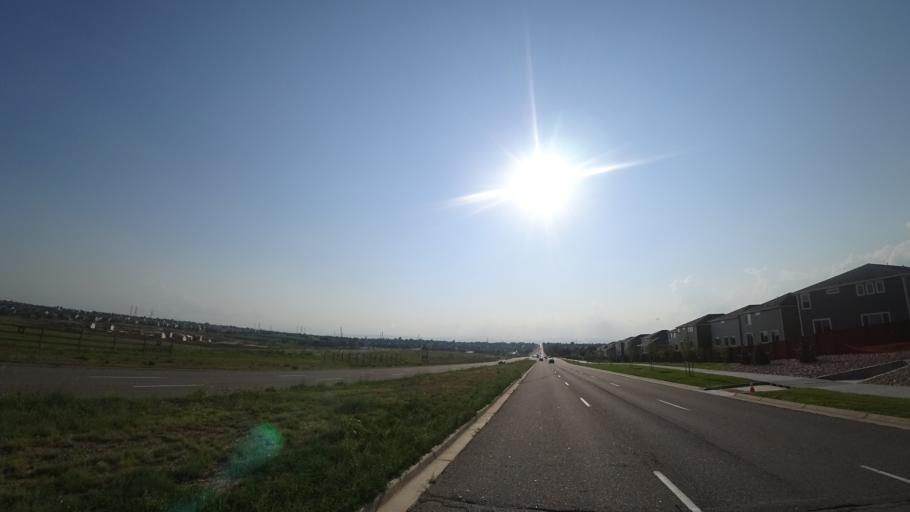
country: US
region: Colorado
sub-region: Arapahoe County
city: Dove Valley
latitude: 39.6385
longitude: -104.7383
